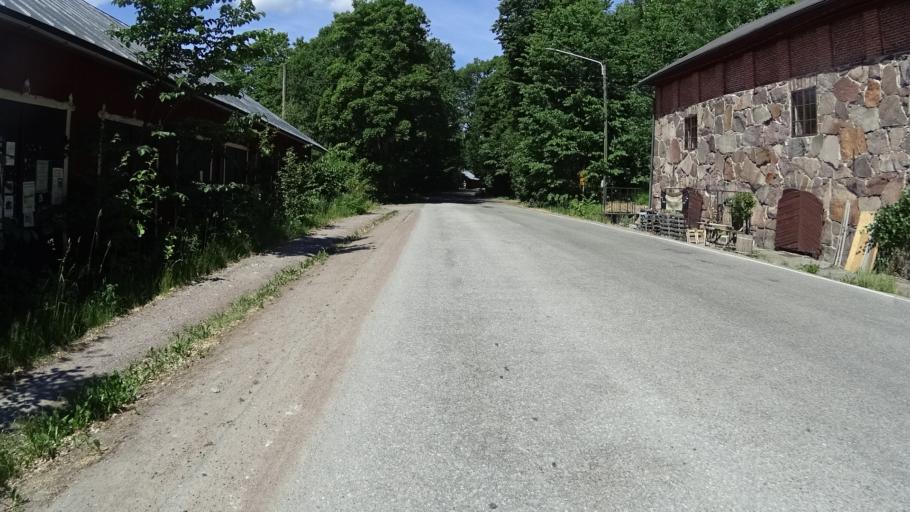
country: FI
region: Uusimaa
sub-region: Raaseporin
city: Karis
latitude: 60.0884
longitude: 23.6389
